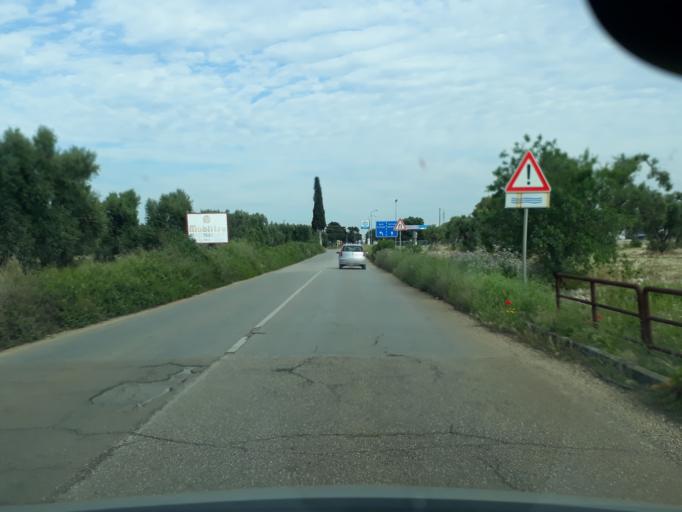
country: IT
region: Apulia
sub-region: Provincia di Brindisi
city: Pezze di Greco
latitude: 40.8070
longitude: 17.4255
